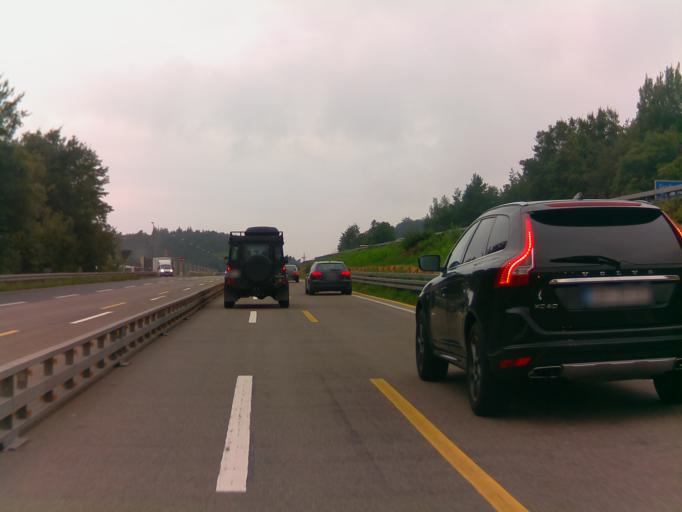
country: DE
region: Hesse
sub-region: Regierungsbezirk Kassel
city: Burghaun
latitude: 50.7104
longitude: 9.6665
